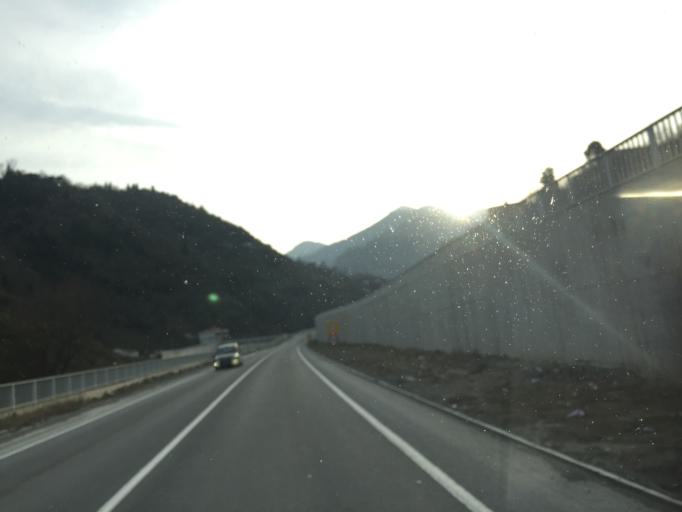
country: TR
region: Trabzon
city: Macka
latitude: 40.8068
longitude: 39.5980
